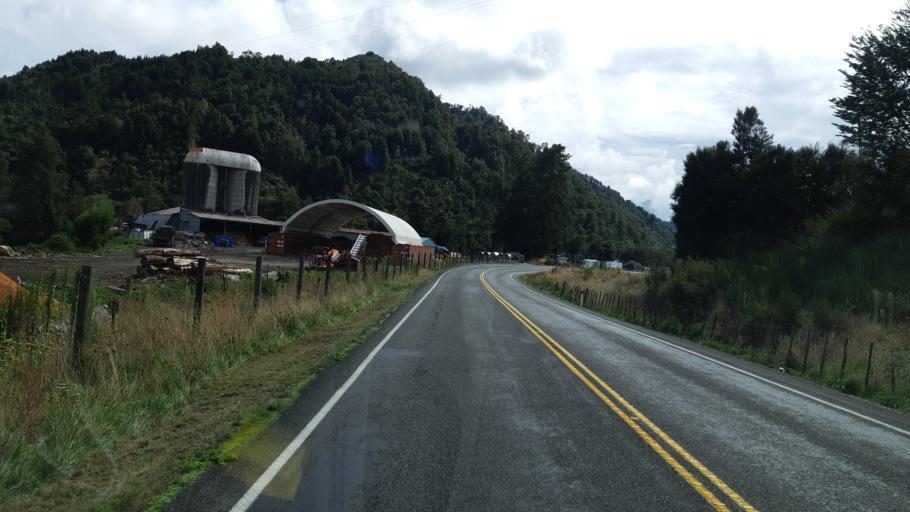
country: NZ
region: West Coast
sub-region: Buller District
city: Westport
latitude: -41.7930
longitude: 172.3655
